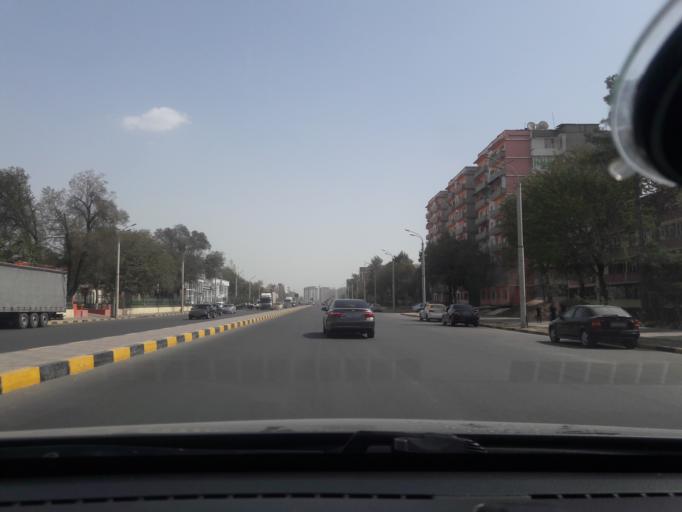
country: TJ
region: Dushanbe
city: Dushanbe
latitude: 38.5584
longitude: 68.7434
